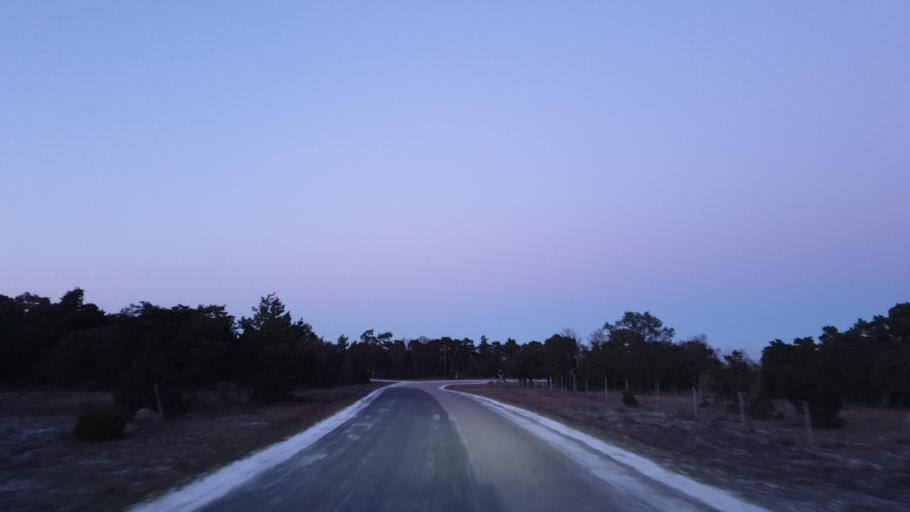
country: SE
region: Gotland
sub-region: Gotland
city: Slite
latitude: 57.4161
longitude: 18.8141
